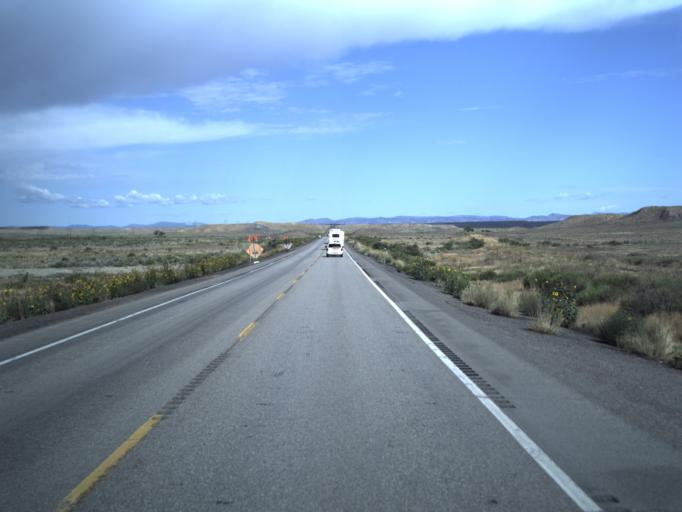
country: US
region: Utah
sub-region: Carbon County
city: East Carbon City
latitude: 39.4583
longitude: -110.4842
